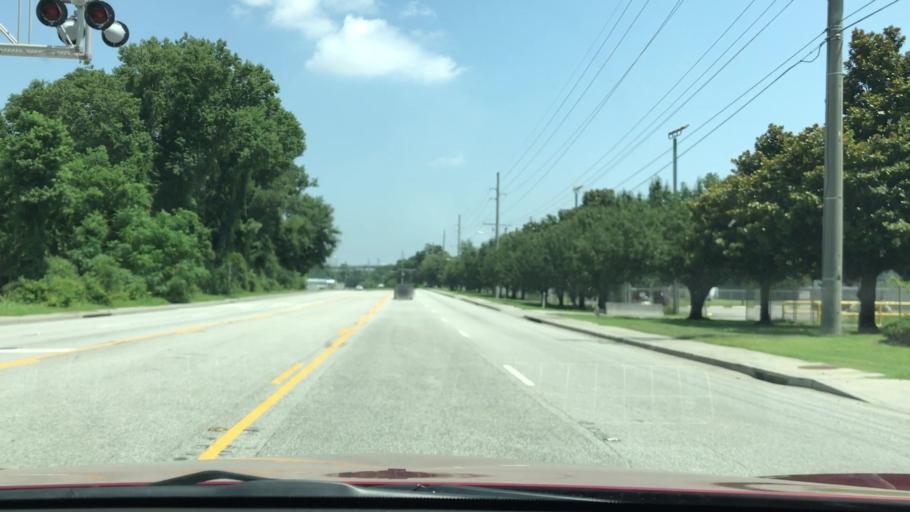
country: US
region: South Carolina
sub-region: Charleston County
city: North Charleston
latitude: 32.8846
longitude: -79.9737
